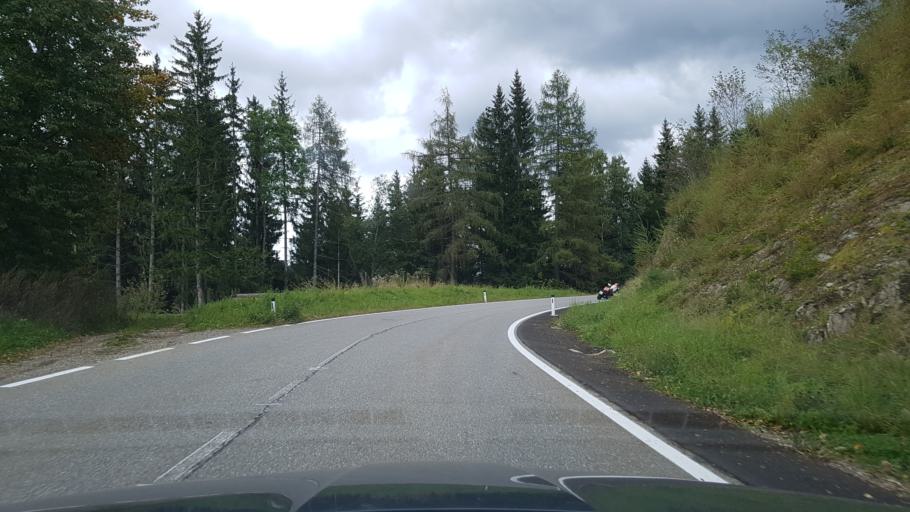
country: AT
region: Styria
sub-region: Politischer Bezirk Murtal
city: Kleinlobming
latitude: 47.1367
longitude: 14.8581
